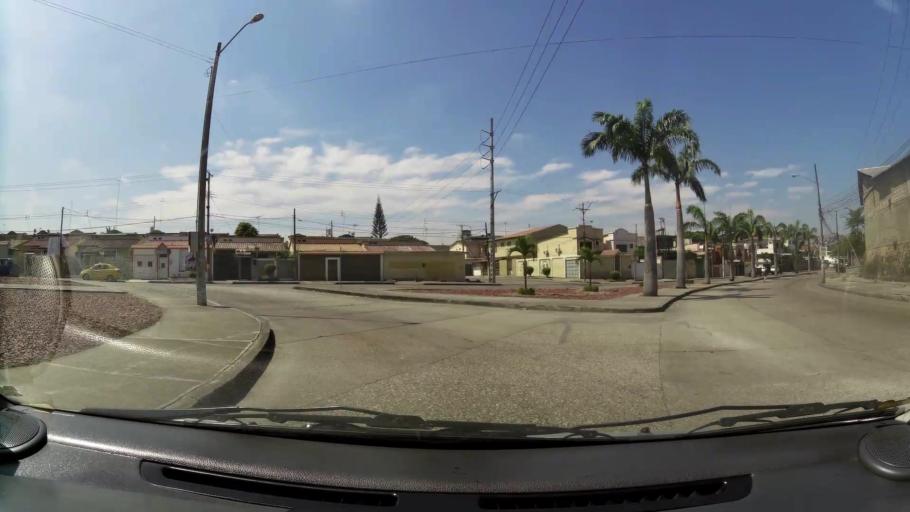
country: EC
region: Guayas
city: Guayaquil
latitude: -2.1312
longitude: -79.9301
